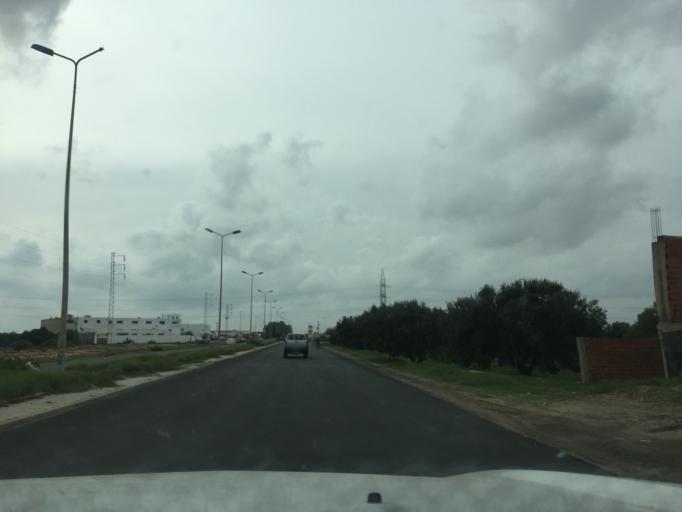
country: TN
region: Susah
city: Masakin
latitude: 35.6856
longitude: 10.5776
